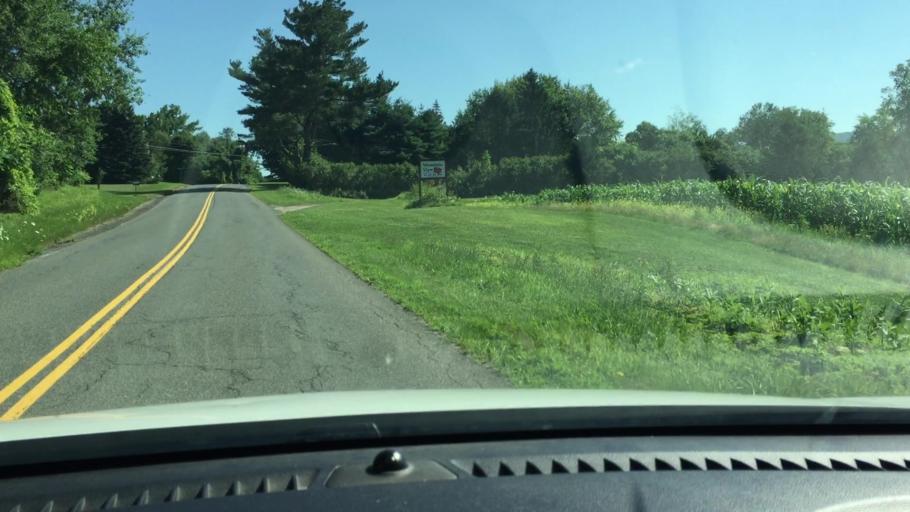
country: US
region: Massachusetts
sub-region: Berkshire County
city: Lanesborough
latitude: 42.5146
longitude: -73.2166
